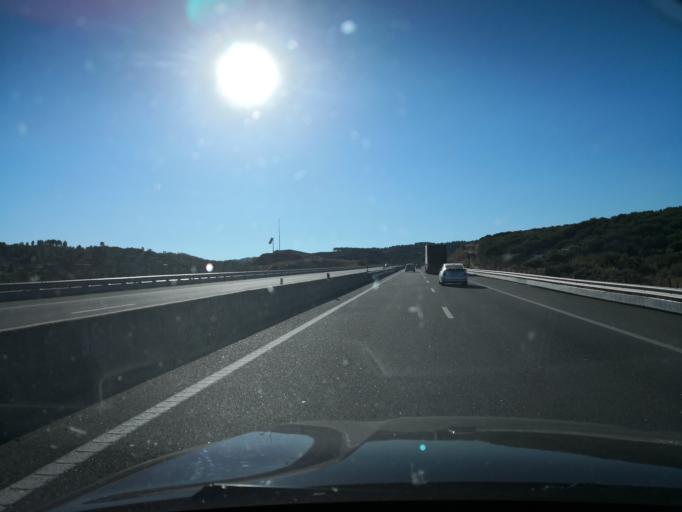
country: PT
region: Vila Real
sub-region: Murca
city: Murca
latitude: 41.3888
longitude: -7.4606
